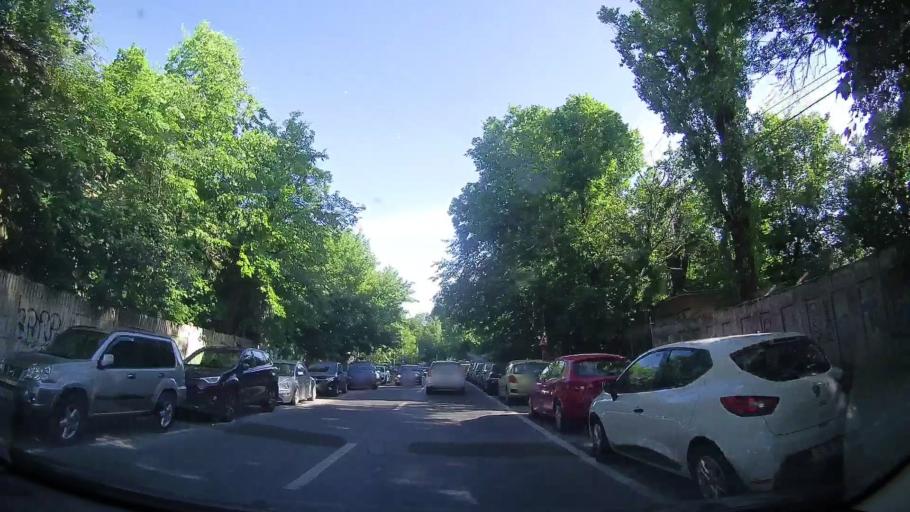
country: RO
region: Bucuresti
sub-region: Municipiul Bucuresti
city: Bucuresti
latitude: 44.4156
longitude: 26.0977
